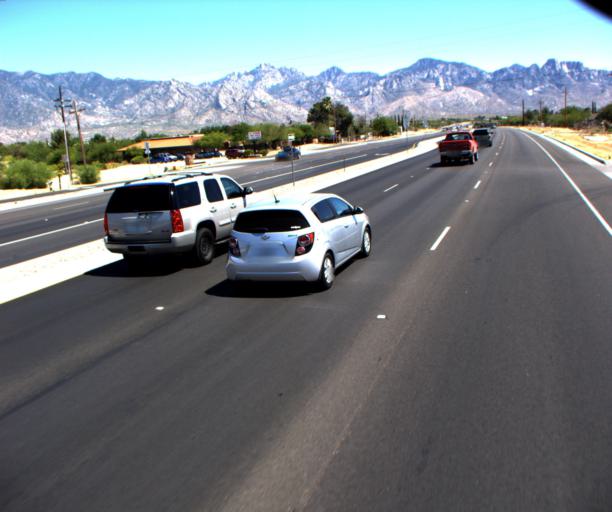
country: US
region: Arizona
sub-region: Pima County
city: Catalina
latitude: 32.4940
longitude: -110.9257
